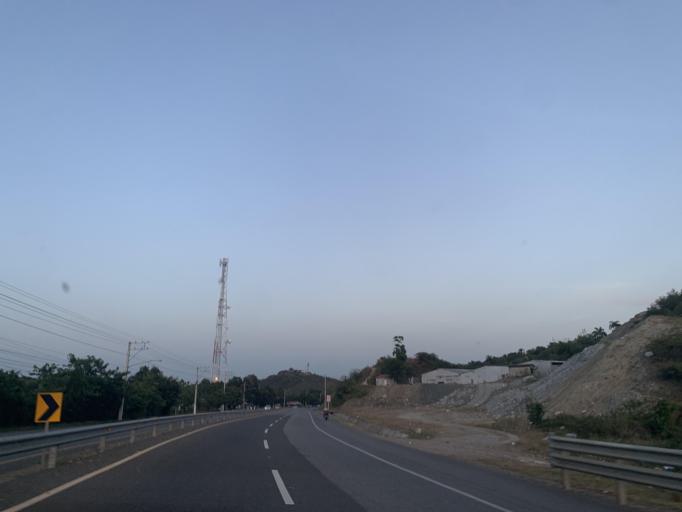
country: DO
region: Puerto Plata
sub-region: Puerto Plata
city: Puerto Plata
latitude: 19.8277
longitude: -70.7508
